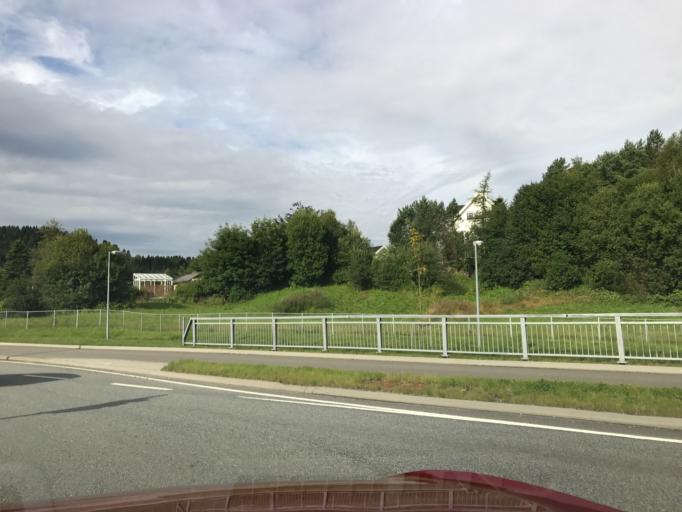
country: NO
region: Hordaland
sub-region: Bergen
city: Hylkje
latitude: 60.4843
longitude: 5.3751
